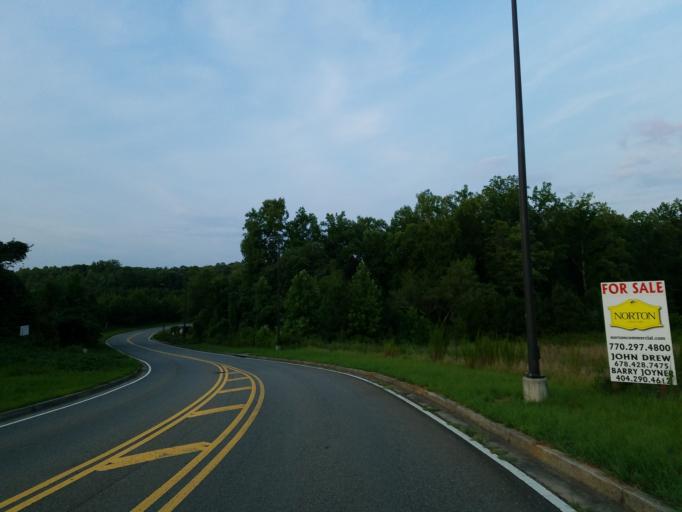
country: US
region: Georgia
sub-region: Pickens County
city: Jasper
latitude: 34.4687
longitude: -84.4554
